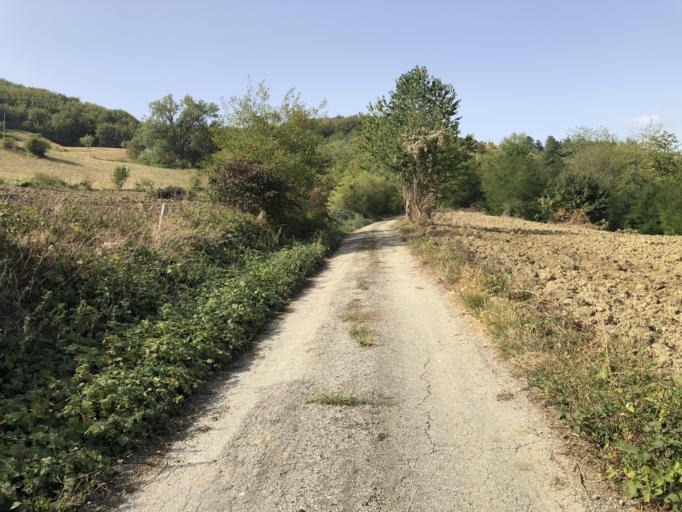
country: IT
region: Emilia-Romagna
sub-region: Forli-Cesena
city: Portico e San Benedetto
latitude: 44.0180
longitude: 11.7883
